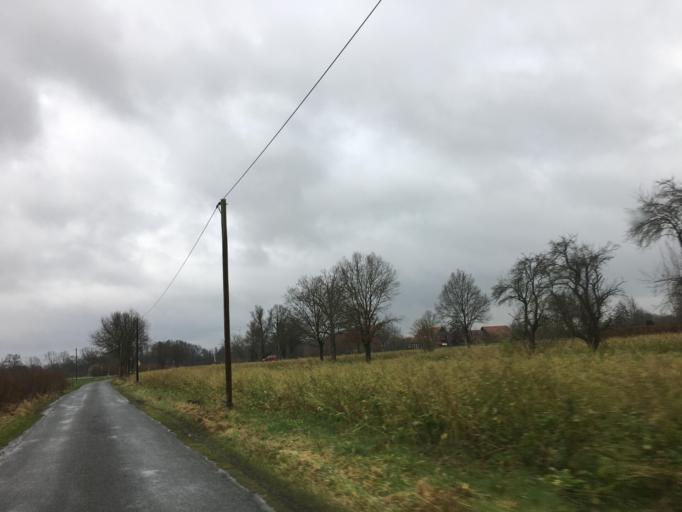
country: DE
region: North Rhine-Westphalia
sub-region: Regierungsbezirk Munster
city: Nordwalde
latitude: 52.0841
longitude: 7.5148
